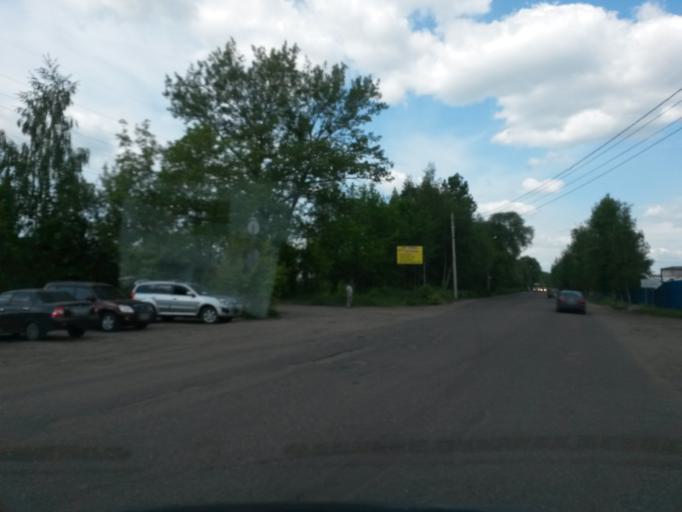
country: RU
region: Jaroslavl
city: Yaroslavl
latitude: 57.5776
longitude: 39.8867
